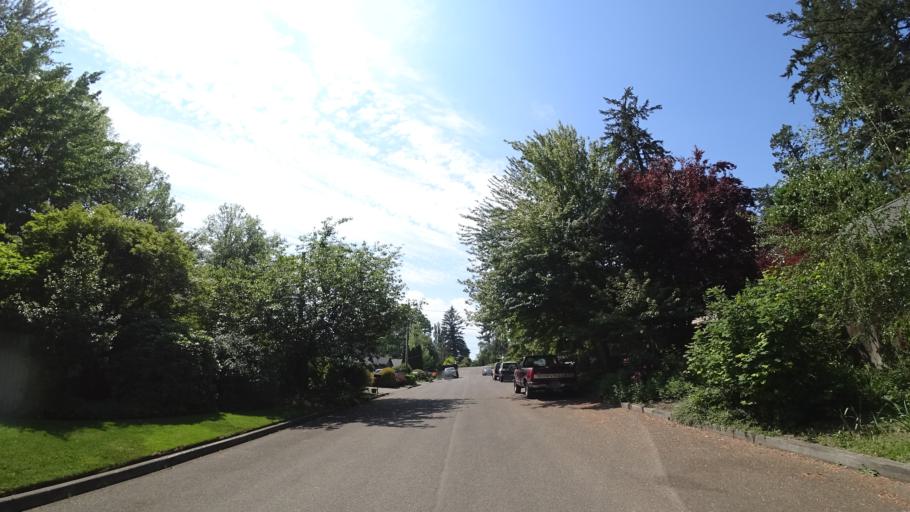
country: US
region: Oregon
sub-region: Washington County
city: Metzger
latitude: 45.4433
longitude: -122.7234
